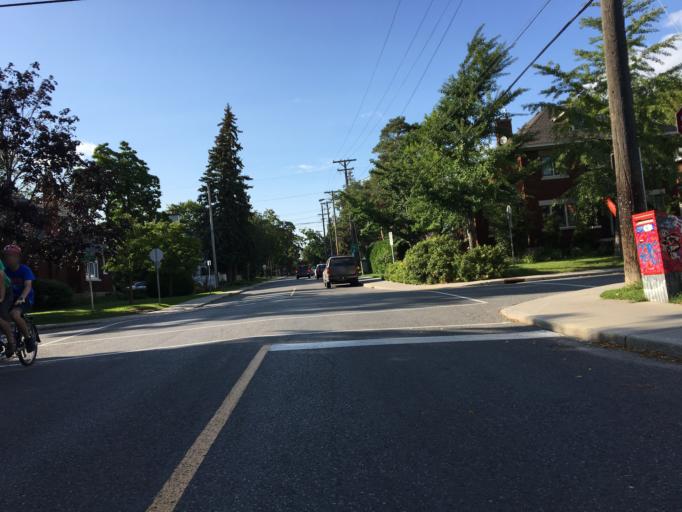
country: CA
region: Ontario
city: Ottawa
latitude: 45.4011
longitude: -75.6946
